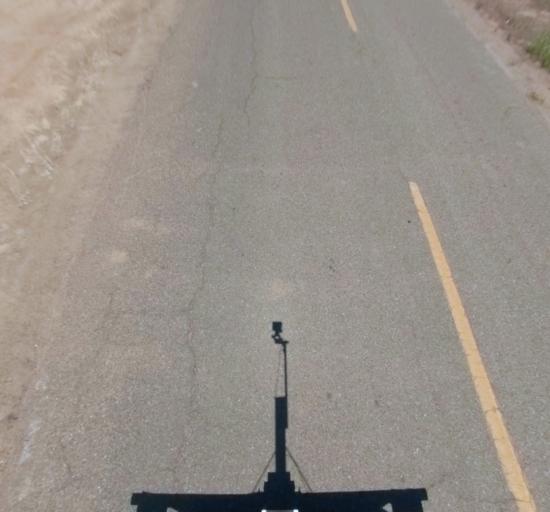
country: US
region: California
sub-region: Madera County
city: Chowchilla
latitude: 37.0898
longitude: -120.2837
